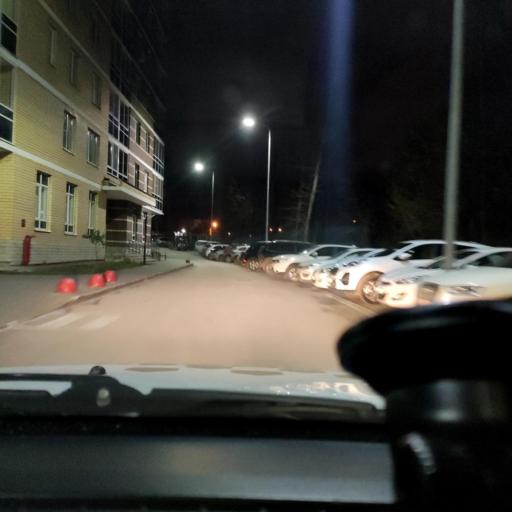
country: RU
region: Perm
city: Perm
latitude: 57.9913
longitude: 56.1917
